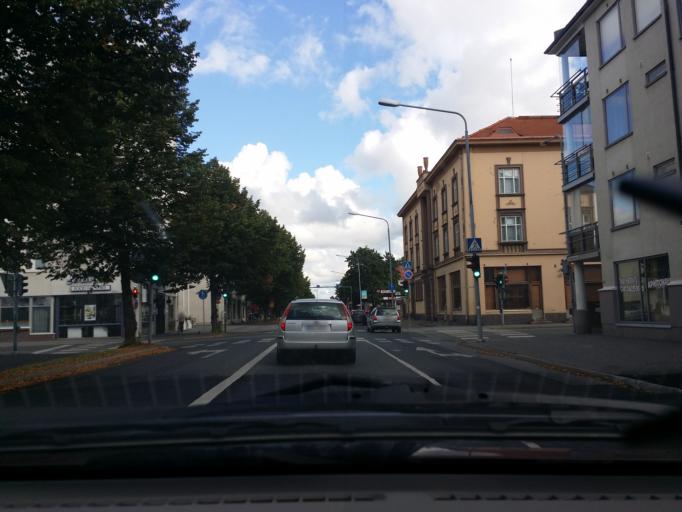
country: FI
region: Satakunta
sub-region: Pori
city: Pori
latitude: 61.4822
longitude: 21.7930
